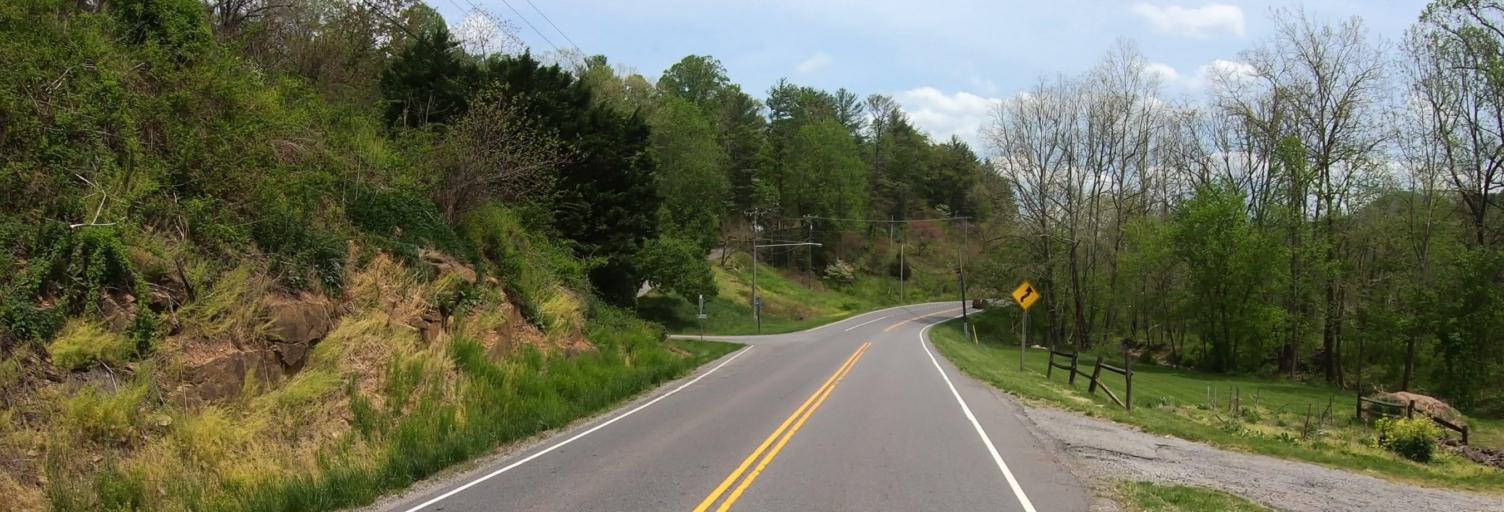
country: US
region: Virginia
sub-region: Roanoke County
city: Cave Spring
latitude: 37.1999
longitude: -80.0681
